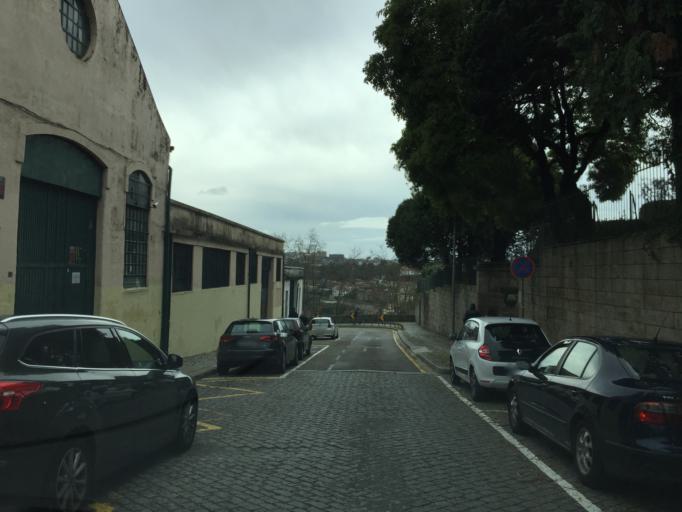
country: PT
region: Porto
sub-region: Porto
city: Porto
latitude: 41.1462
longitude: -8.6246
